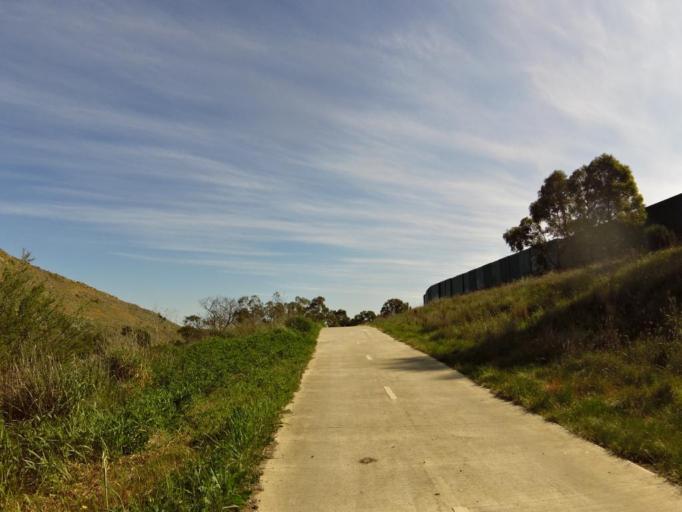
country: AU
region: Victoria
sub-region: Brimbank
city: Brooklyn
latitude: -37.8078
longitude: 144.8329
